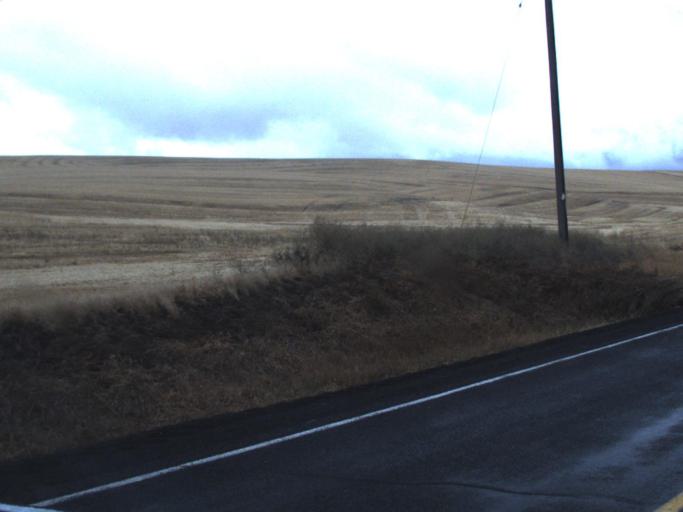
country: US
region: Washington
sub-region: Whitman County
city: Colfax
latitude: 47.0602
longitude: -117.5228
